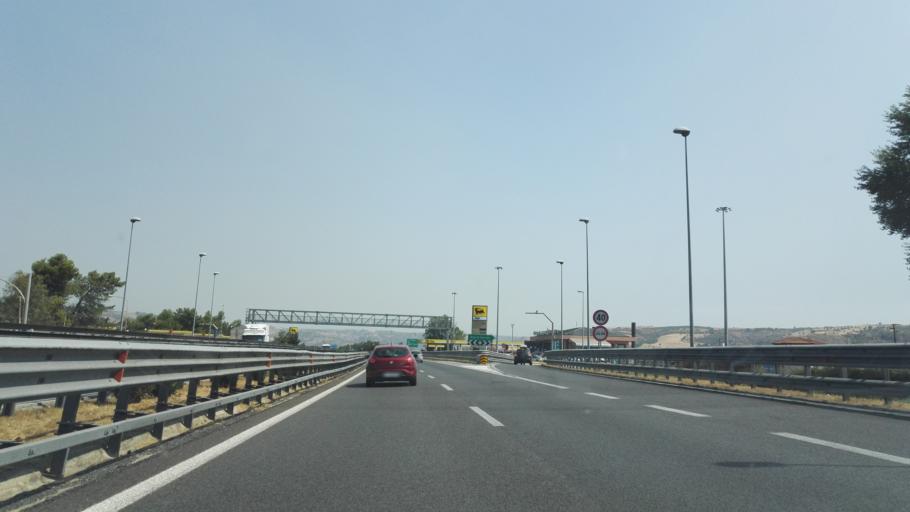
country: IT
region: Calabria
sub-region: Provincia di Cosenza
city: Tarsia
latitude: 39.5772
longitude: 16.2422
